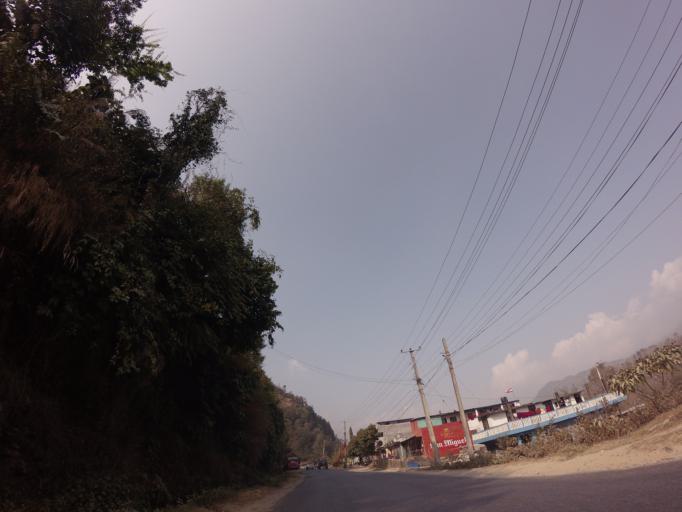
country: NP
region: Western Region
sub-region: Gandaki Zone
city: Pokhara
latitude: 28.2481
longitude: 83.9758
